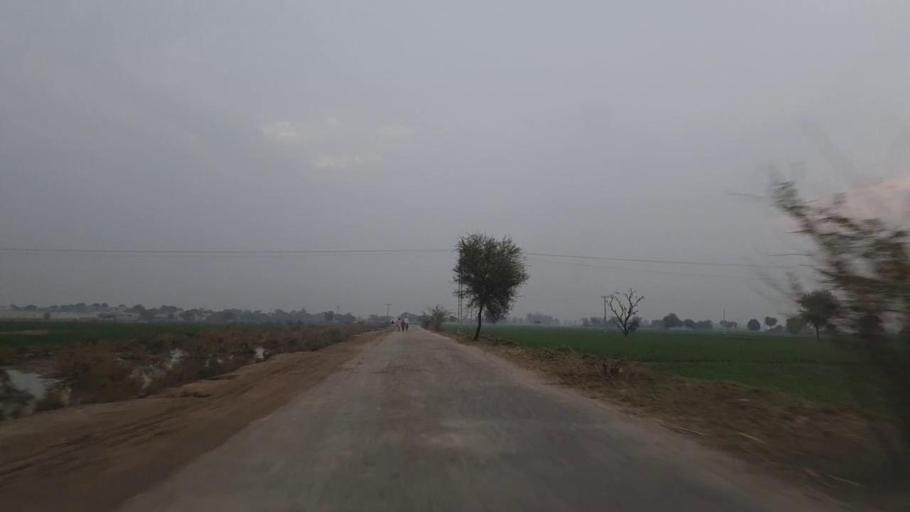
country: PK
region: Sindh
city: Jam Sahib
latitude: 26.3398
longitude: 68.5641
